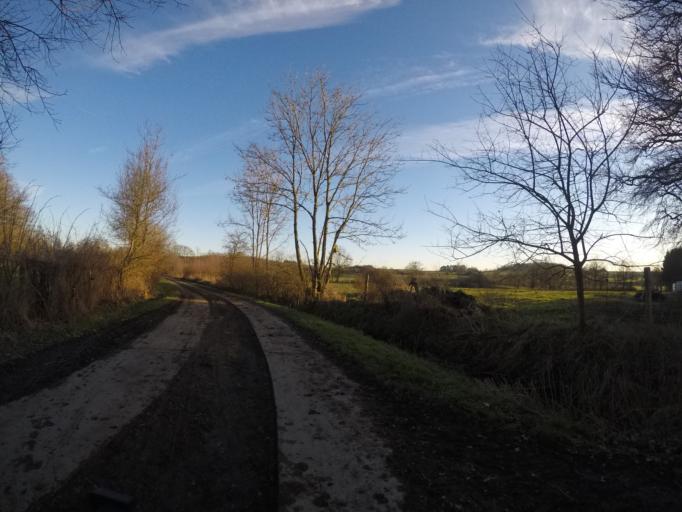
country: BE
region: Wallonia
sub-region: Province du Luxembourg
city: Habay-la-Vieille
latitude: 49.7233
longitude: 5.6016
